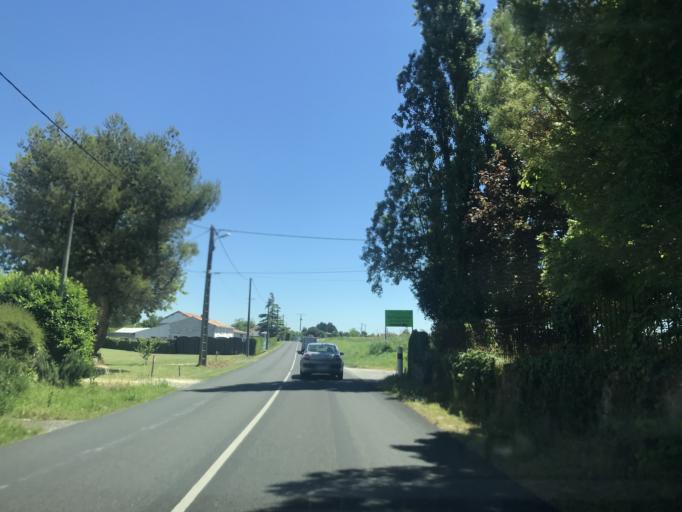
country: FR
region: Poitou-Charentes
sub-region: Departement de la Charente-Maritime
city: Meschers-sur-Gironde
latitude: 45.5882
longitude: -0.9621
